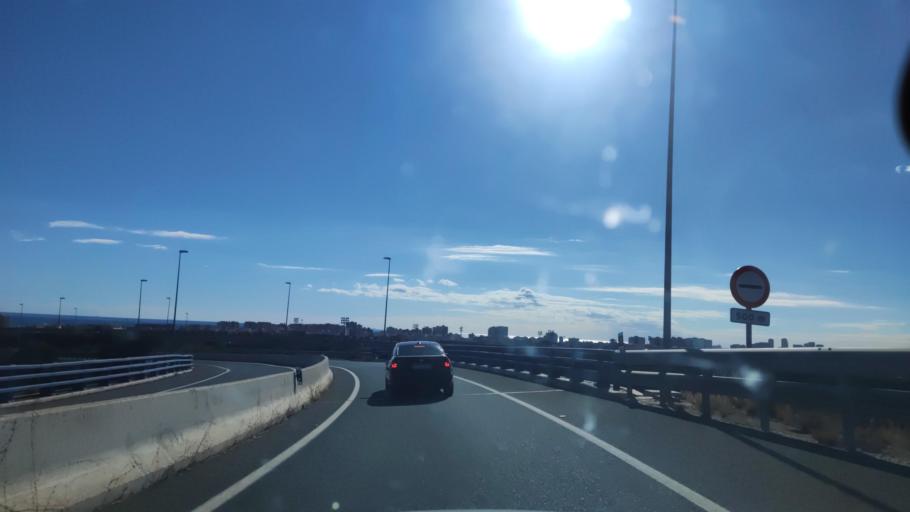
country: ES
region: Valencia
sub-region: Provincia de Alicante
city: el Campello
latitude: 38.4390
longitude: -0.4052
